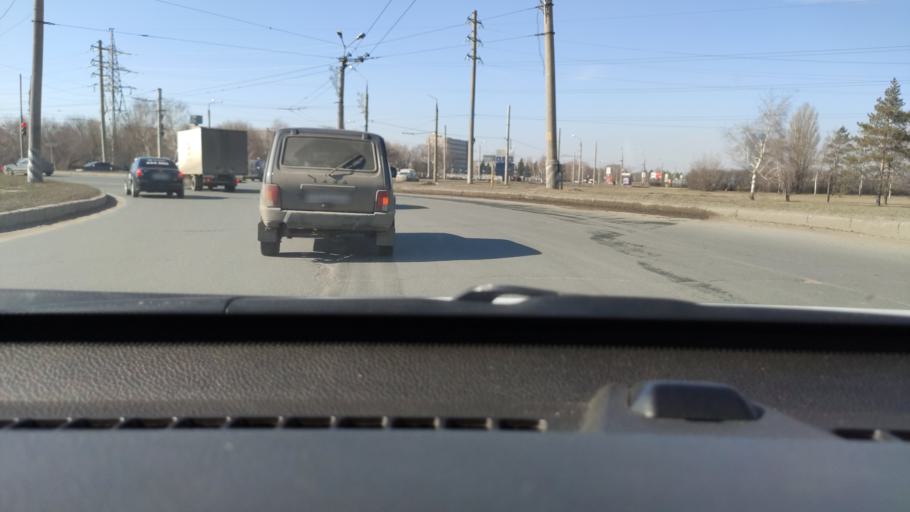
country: RU
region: Samara
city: Tol'yatti
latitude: 53.5515
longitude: 49.2971
